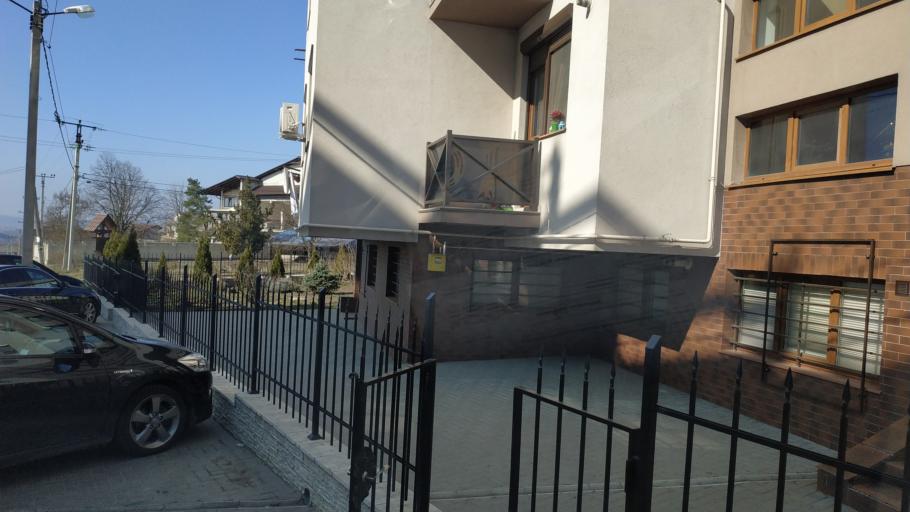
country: MD
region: Chisinau
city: Vatra
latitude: 47.0158
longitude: 28.7459
